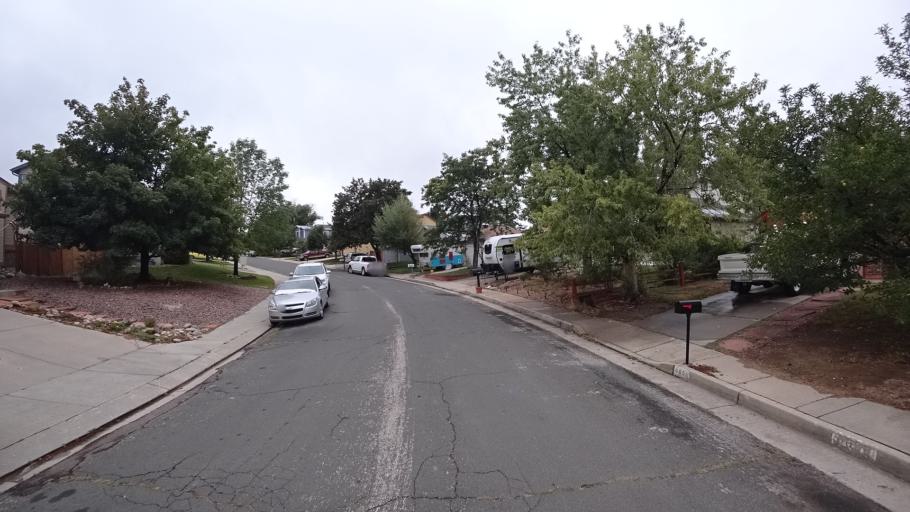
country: US
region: Colorado
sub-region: El Paso County
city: Cimarron Hills
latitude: 38.9284
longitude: -104.7647
